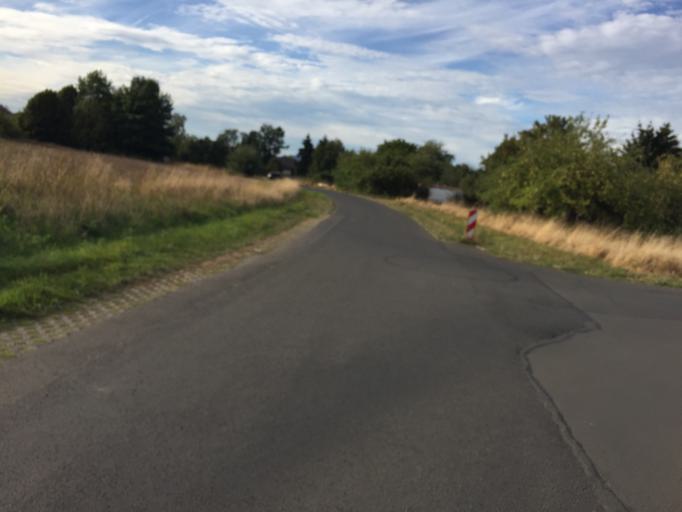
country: DE
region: Hesse
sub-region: Regierungsbezirk Giessen
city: Langgons
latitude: 50.5298
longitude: 8.7130
